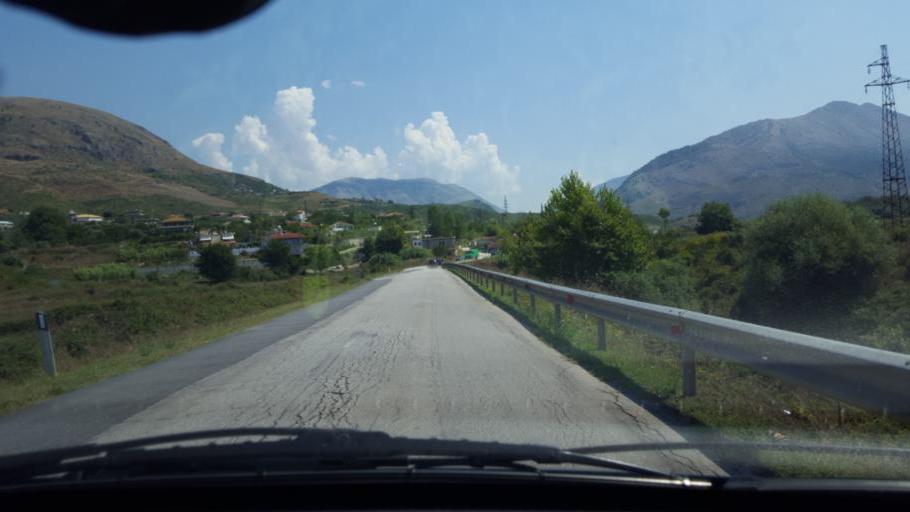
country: AL
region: Vlore
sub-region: Rrethi i Delvines
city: Mesopotam
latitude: 39.9106
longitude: 20.0998
